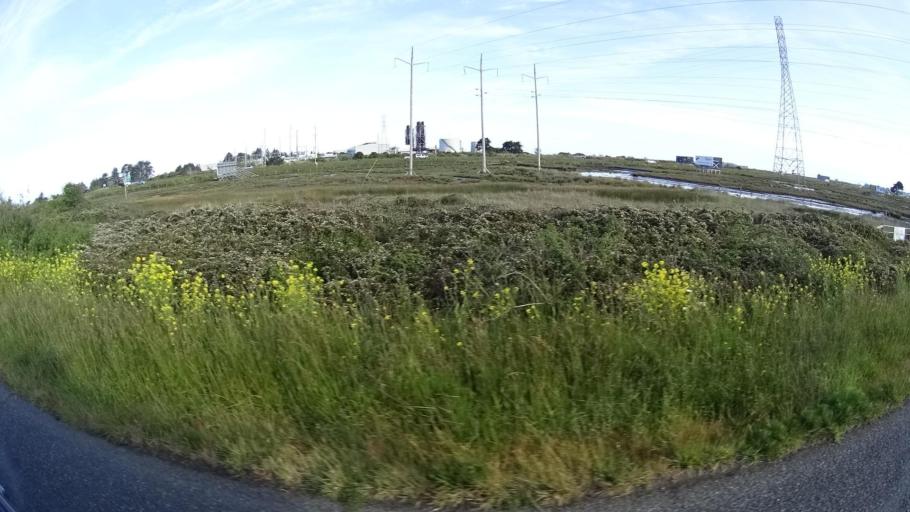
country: US
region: California
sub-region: Humboldt County
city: Humboldt Hill
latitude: 40.7387
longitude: -124.2050
